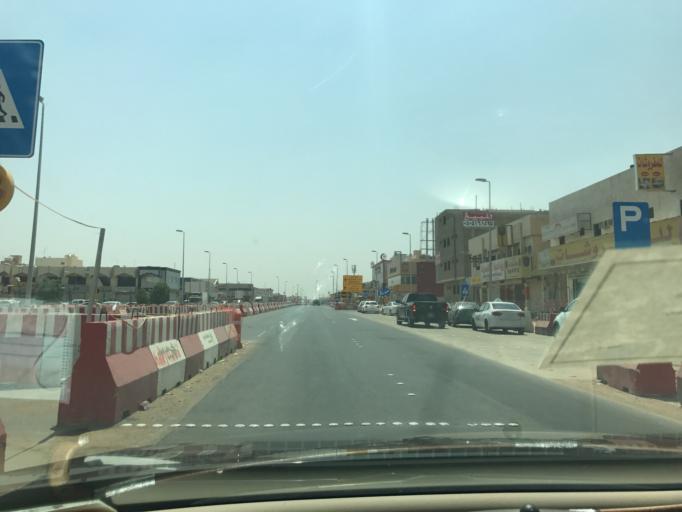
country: SA
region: Ar Riyad
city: Riyadh
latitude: 24.7490
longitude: 46.7730
